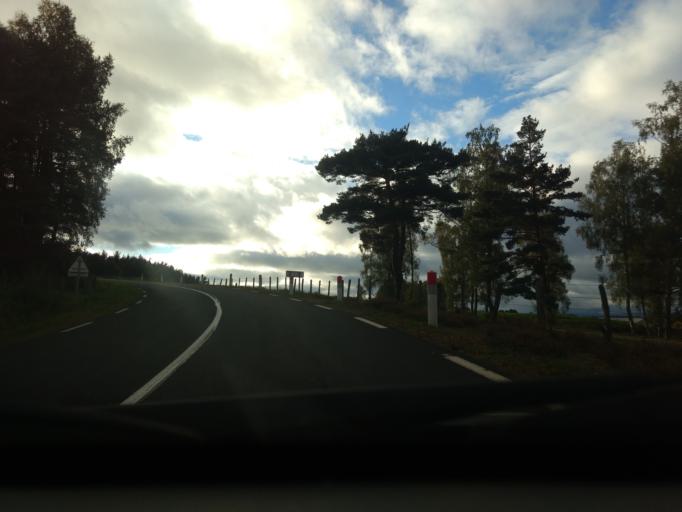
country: FR
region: Auvergne
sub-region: Departement du Cantal
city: Chaudes-Aigues
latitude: 44.8188
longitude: 2.9651
